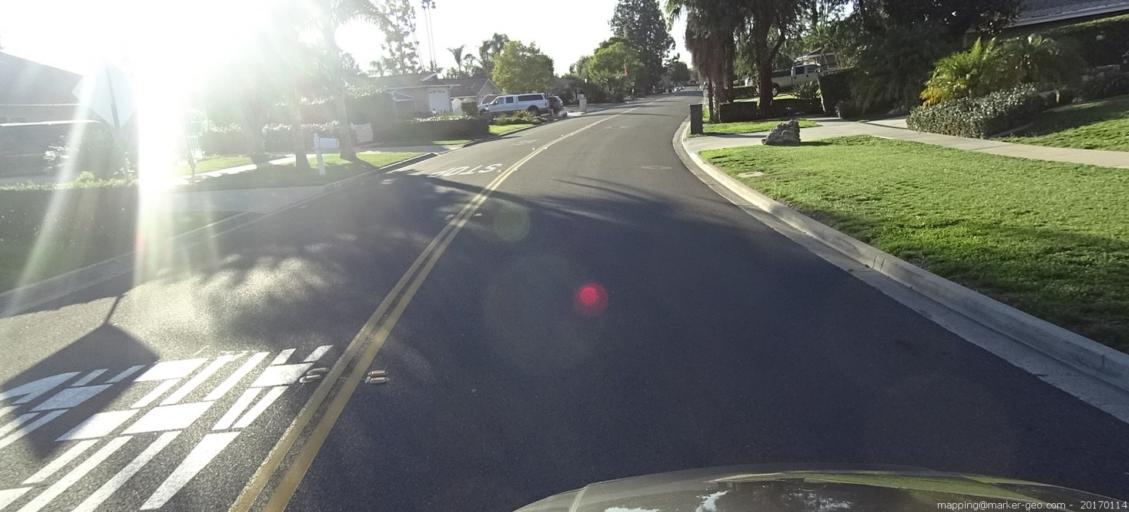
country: US
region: California
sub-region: Orange County
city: North Tustin
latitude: 33.7669
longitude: -117.8141
